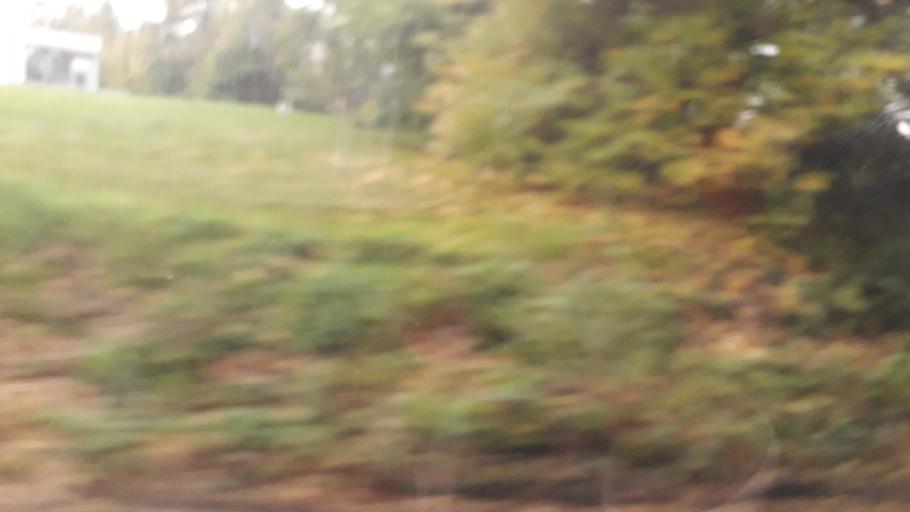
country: IE
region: Munster
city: Ballina
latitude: 52.7964
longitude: -8.4347
